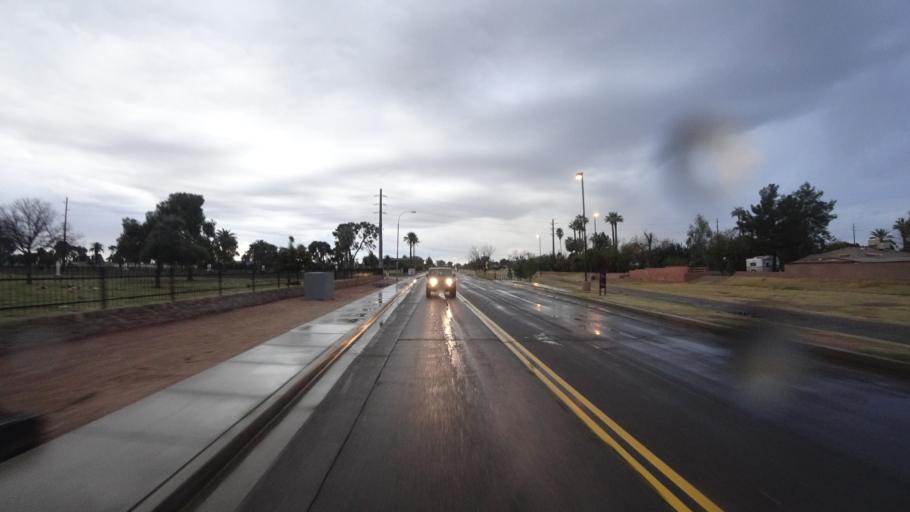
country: US
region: Arizona
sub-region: Maricopa County
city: Paradise Valley
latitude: 33.4735
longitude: -111.9781
